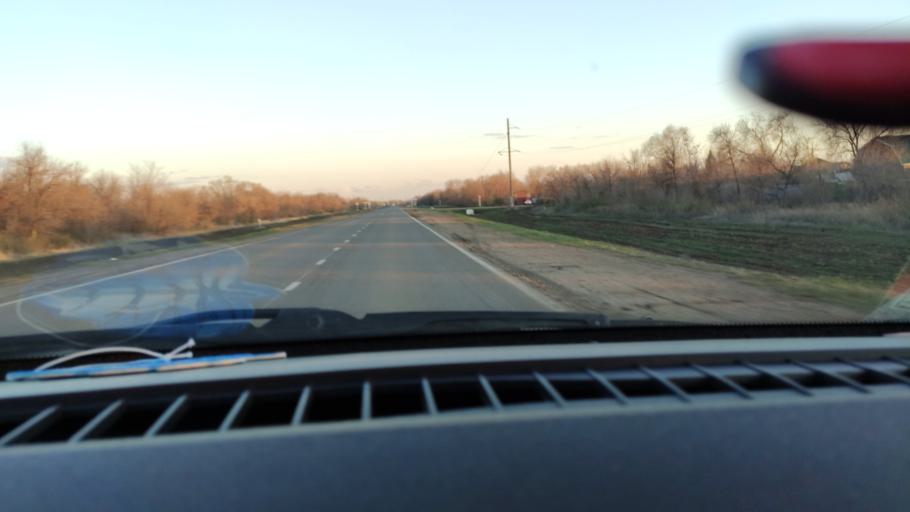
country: RU
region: Saratov
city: Privolzhskiy
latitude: 51.3796
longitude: 46.0432
